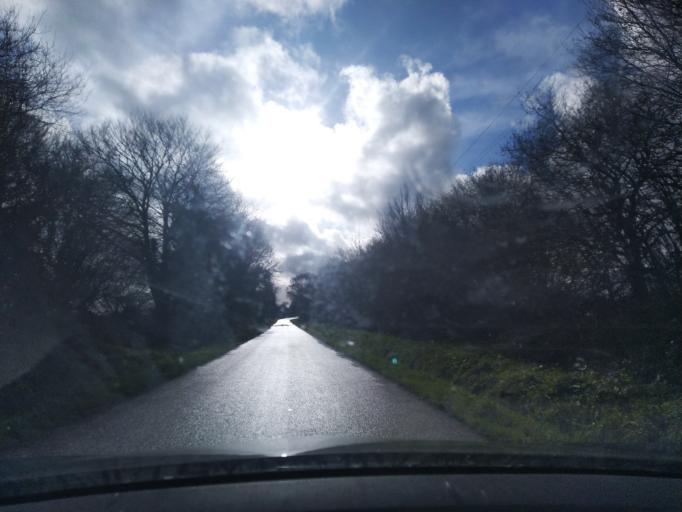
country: FR
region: Brittany
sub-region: Departement du Finistere
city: Guerlesquin
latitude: 48.4605
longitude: -3.5792
